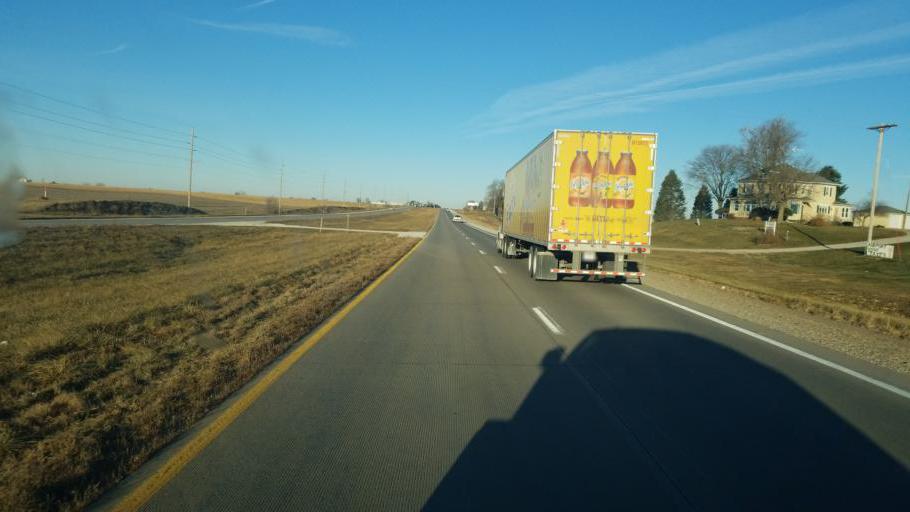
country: US
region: Iowa
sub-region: Marion County
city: Pella
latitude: 41.3720
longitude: -92.8022
